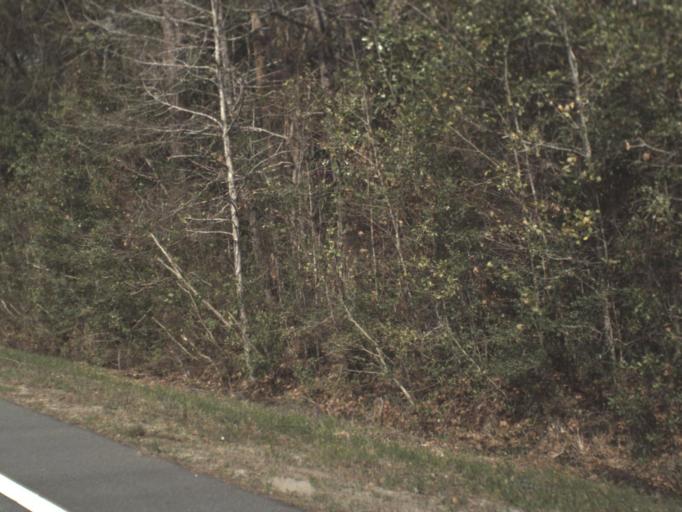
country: US
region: Florida
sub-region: Franklin County
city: Carrabelle
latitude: 29.9925
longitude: -84.5031
